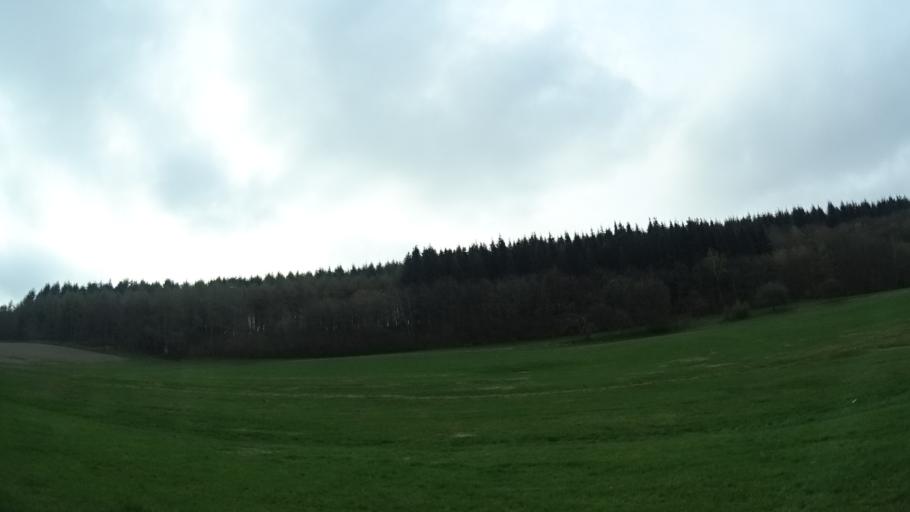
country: DE
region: Rheinland-Pfalz
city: Leisel
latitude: 49.7227
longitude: 7.2139
